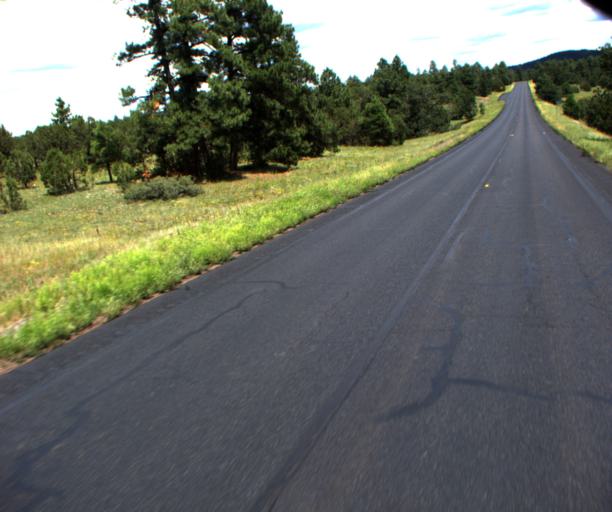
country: US
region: Arizona
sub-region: Gila County
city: Pine
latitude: 34.5176
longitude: -111.5274
